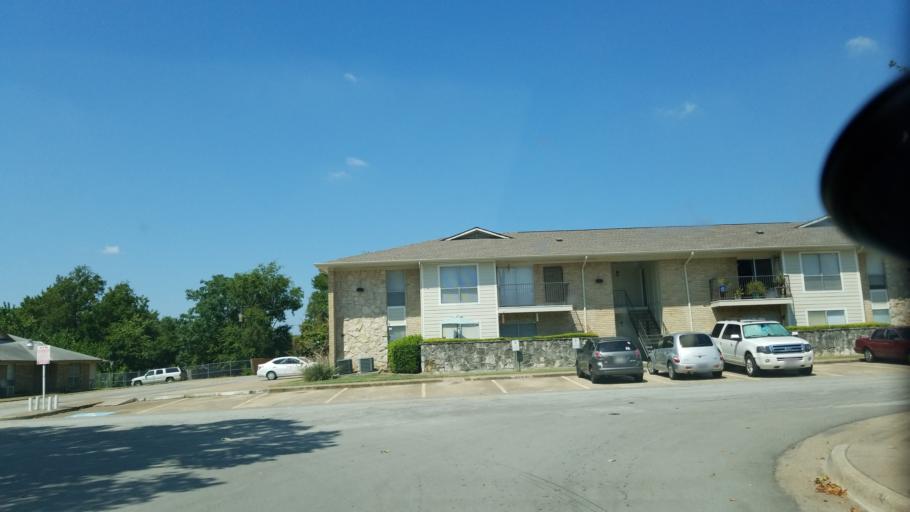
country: US
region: Texas
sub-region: Dallas County
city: Duncanville
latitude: 32.6576
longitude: -96.8948
